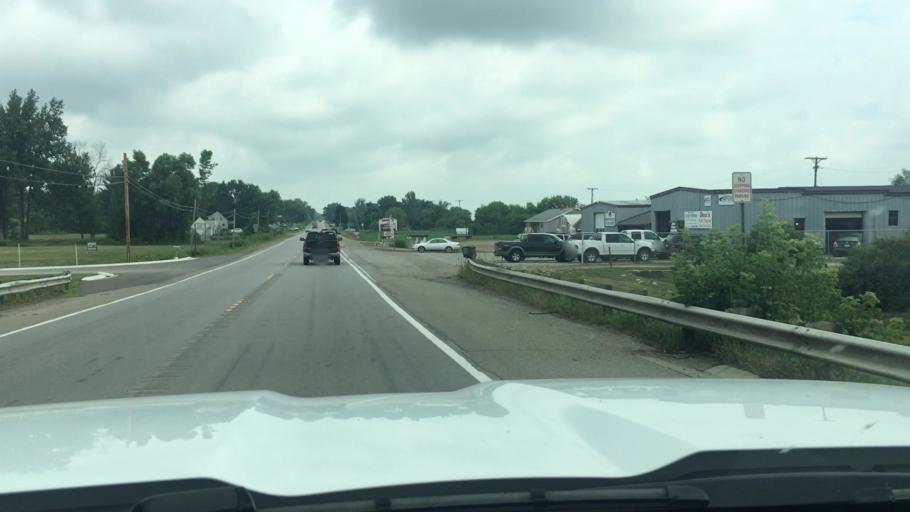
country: US
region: Michigan
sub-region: Lapeer County
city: Imlay City
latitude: 43.0329
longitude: -83.0716
